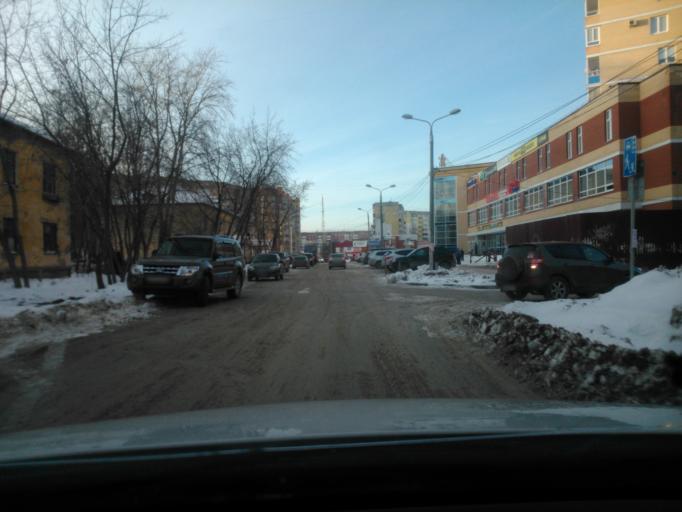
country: RU
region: Perm
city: Perm
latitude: 58.0009
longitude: 56.3044
